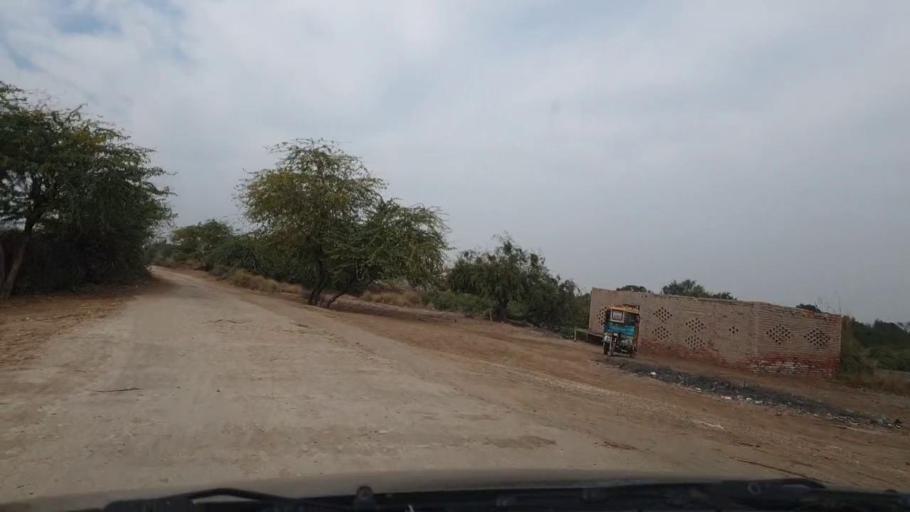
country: PK
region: Sindh
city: Sanghar
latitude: 26.0979
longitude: 68.9000
